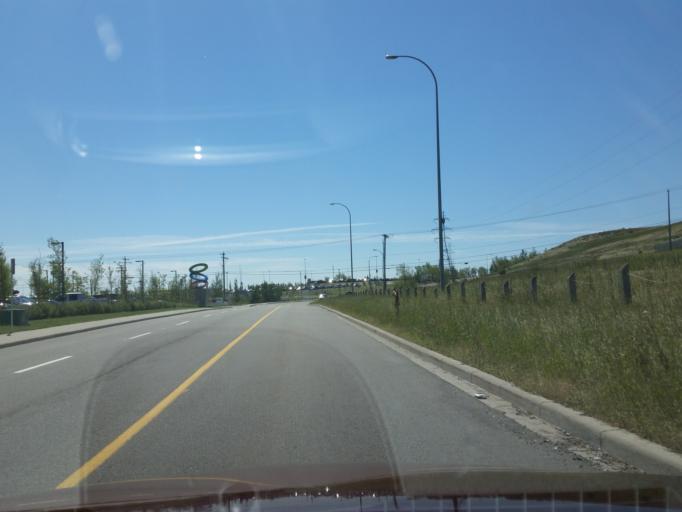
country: CA
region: Alberta
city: Calgary
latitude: 51.0537
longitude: -114.0265
